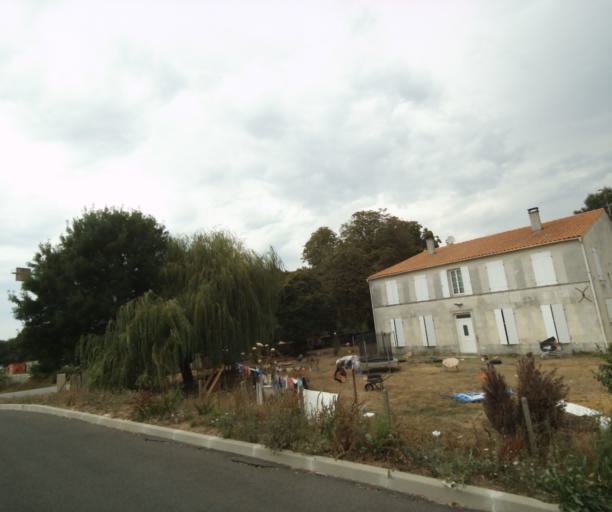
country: FR
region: Poitou-Charentes
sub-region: Departement de la Charente-Maritime
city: Tonnay-Charente
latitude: 45.9517
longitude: -0.8998
